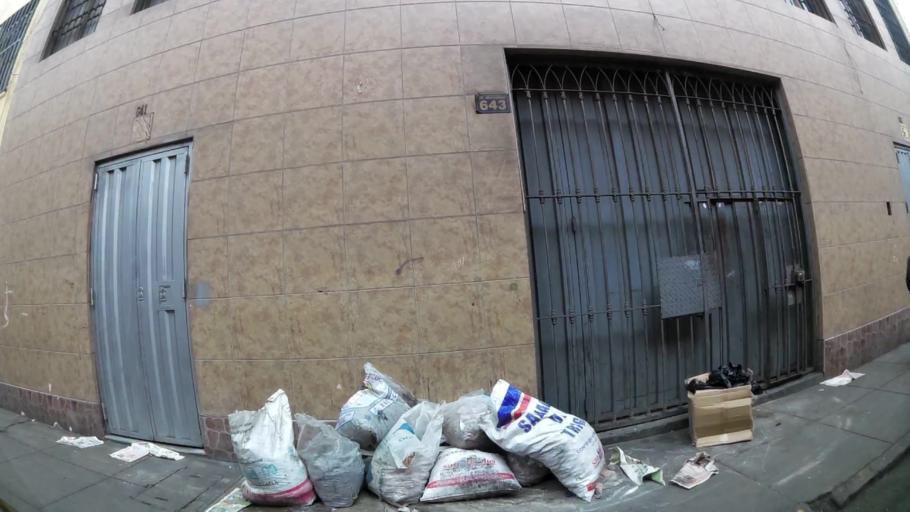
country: PE
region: Lima
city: Lima
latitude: -12.0465
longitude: -77.0396
